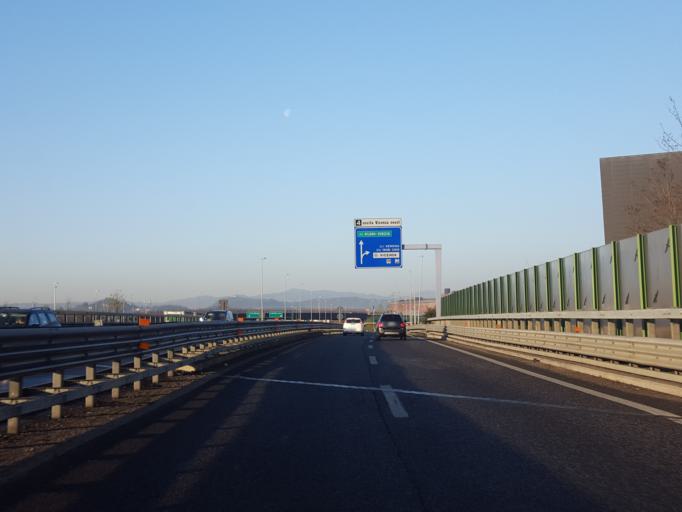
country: IT
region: Veneto
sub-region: Provincia di Vicenza
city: Creazzo
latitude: 45.5181
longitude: 11.5119
